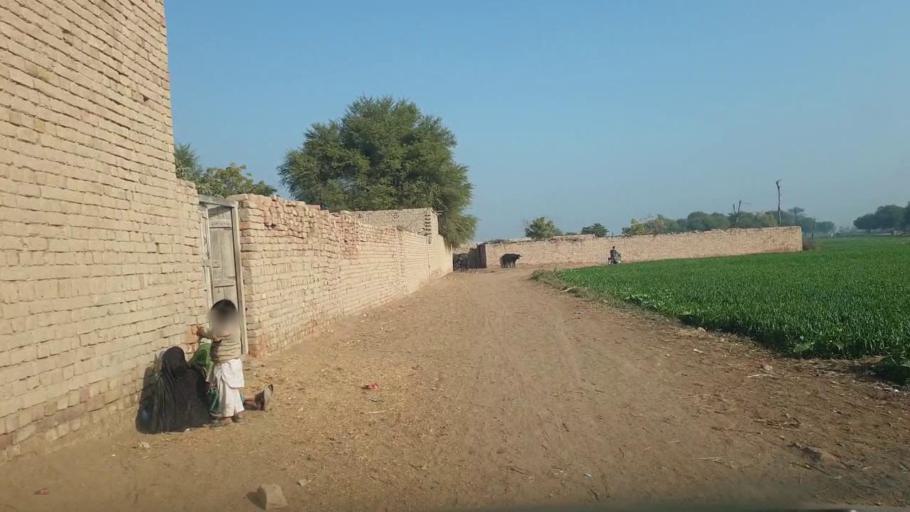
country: PK
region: Sindh
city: Shahdadpur
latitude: 25.9435
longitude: 68.6078
